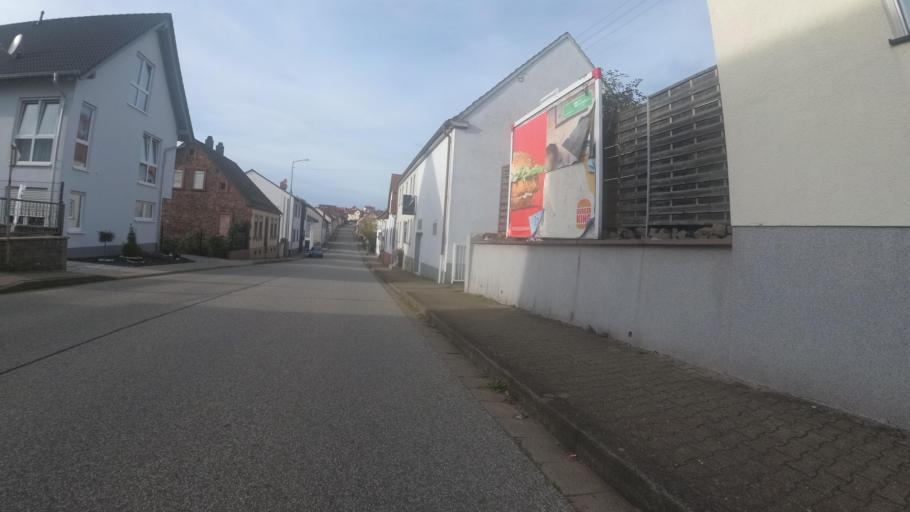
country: DE
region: Rheinland-Pfalz
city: Ramstein-Miesenbach
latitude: 49.4572
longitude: 7.5587
